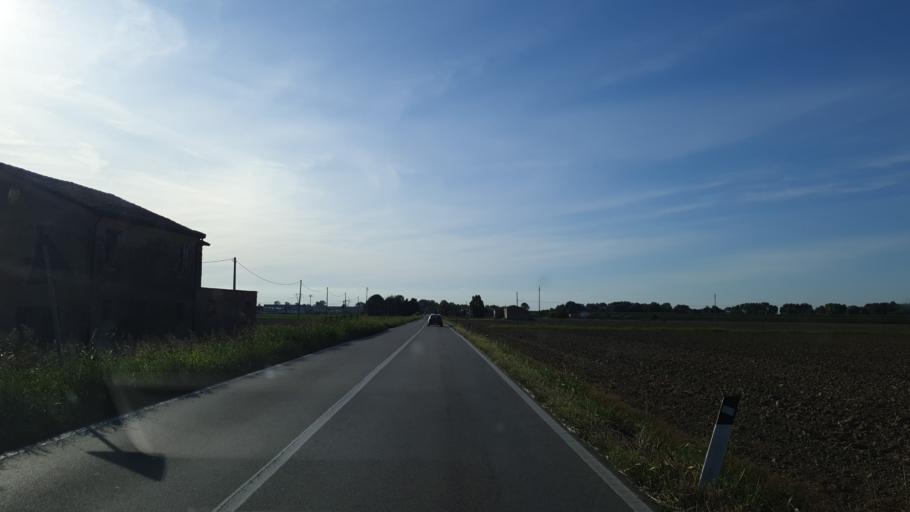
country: IT
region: Emilia-Romagna
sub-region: Provincia di Ravenna
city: Voltana
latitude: 44.5511
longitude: 11.9512
